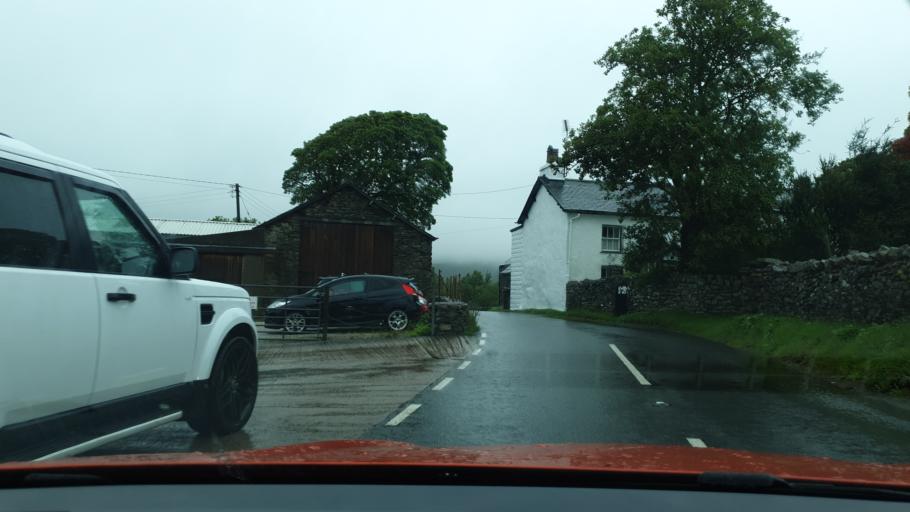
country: GB
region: England
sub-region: Cumbria
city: Ulverston
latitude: 54.3296
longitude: -3.0978
